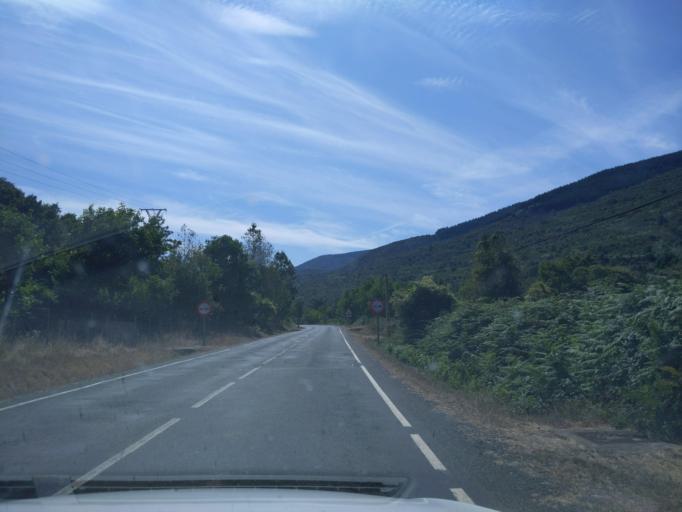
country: ES
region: La Rioja
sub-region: Provincia de La Rioja
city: Ezcaray
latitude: 42.3019
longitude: -3.0241
